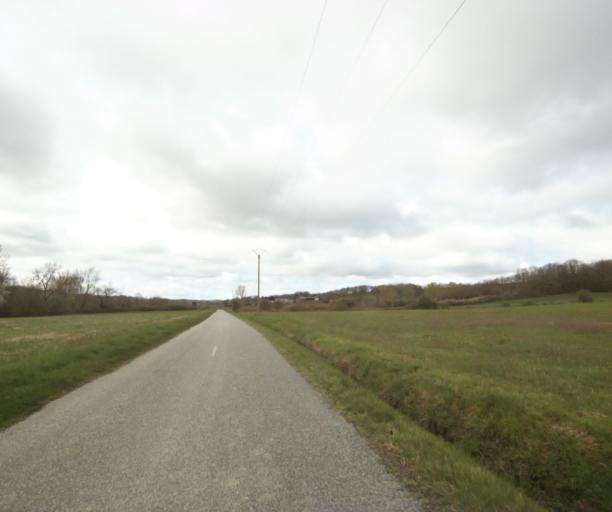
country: FR
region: Midi-Pyrenees
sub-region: Departement de l'Ariege
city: Saverdun
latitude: 43.2225
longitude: 1.5330
